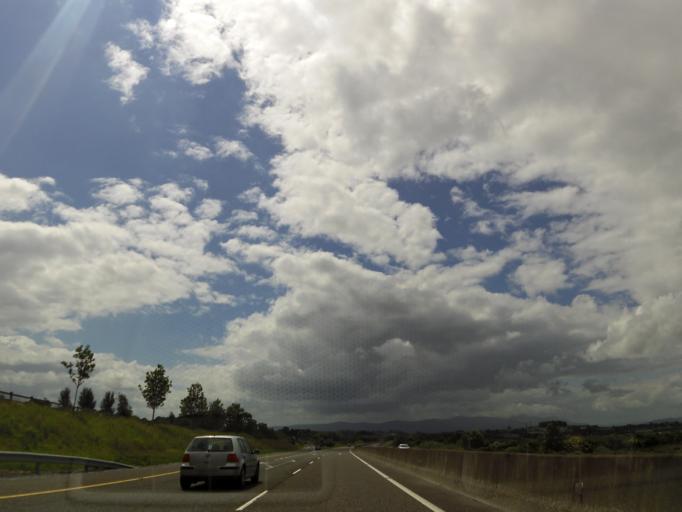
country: IE
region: Munster
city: Cashel
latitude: 52.5136
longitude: -7.8653
